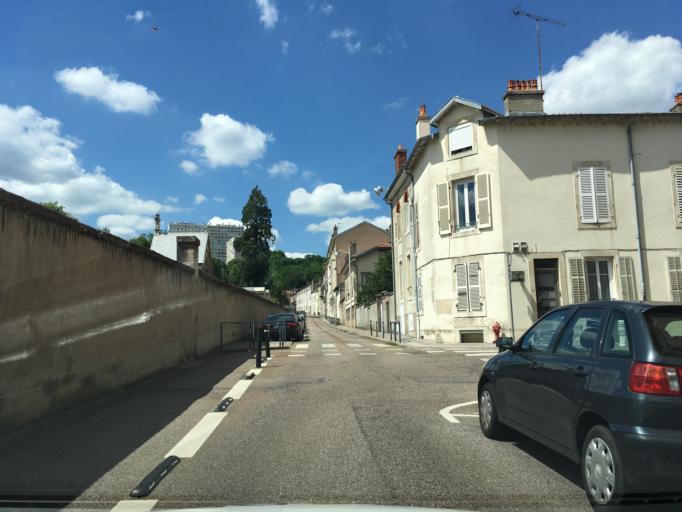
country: FR
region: Lorraine
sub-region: Departement de Meurthe-et-Moselle
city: Maxeville
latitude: 48.6895
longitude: 6.1660
